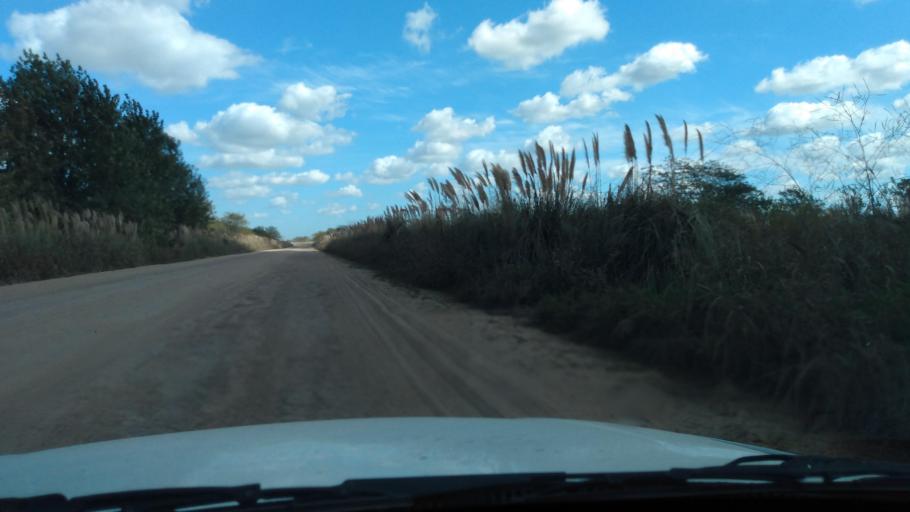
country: AR
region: Buenos Aires
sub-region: Partido de Navarro
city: Navarro
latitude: -35.0000
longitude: -59.3405
